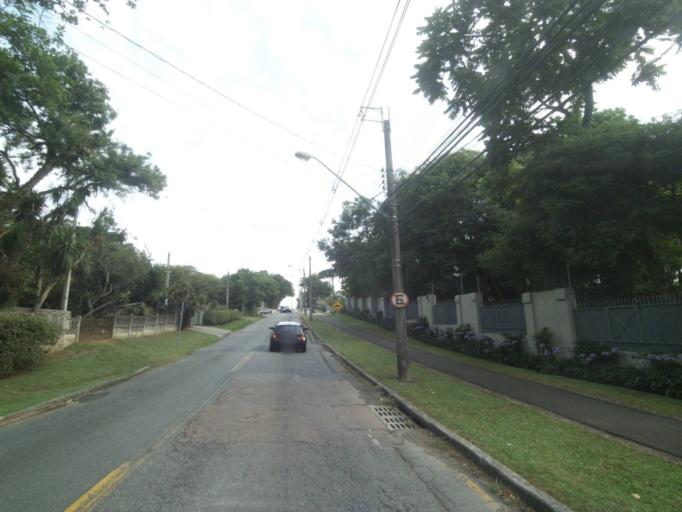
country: BR
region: Parana
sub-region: Curitiba
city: Curitiba
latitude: -25.4190
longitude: -49.3200
